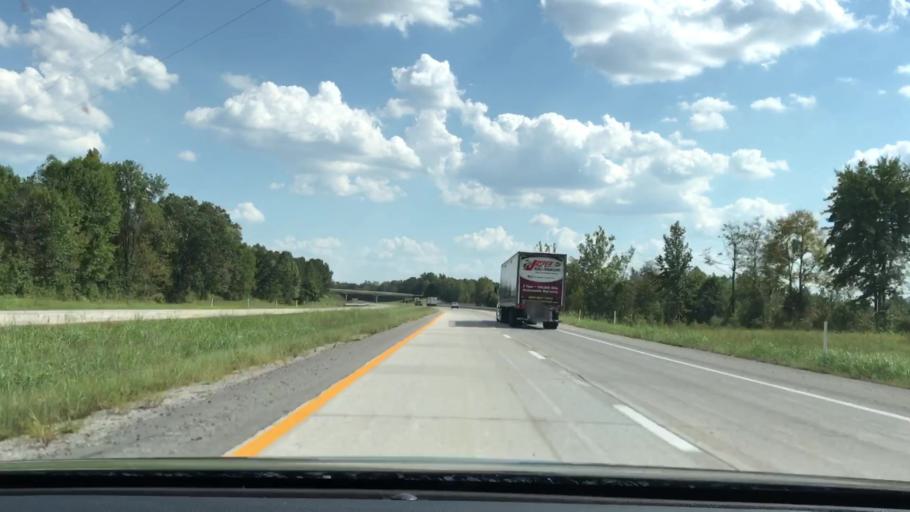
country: US
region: Kentucky
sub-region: Ohio County
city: Oak Grove
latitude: 37.3549
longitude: -86.7887
